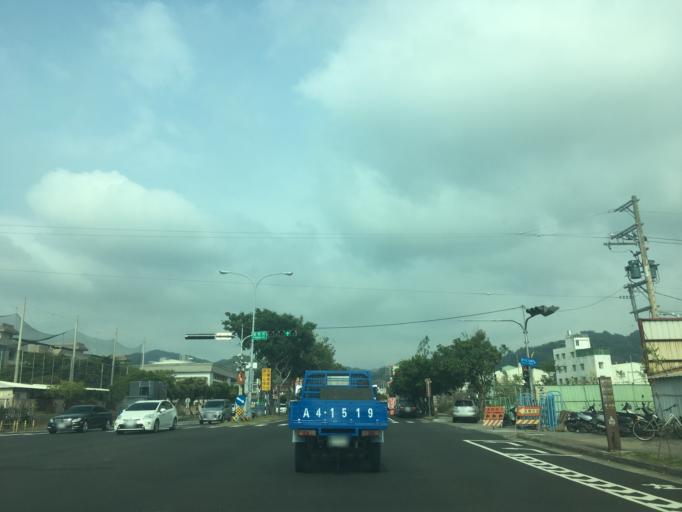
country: TW
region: Taiwan
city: Fengyuan
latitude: 24.2366
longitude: 120.7200
